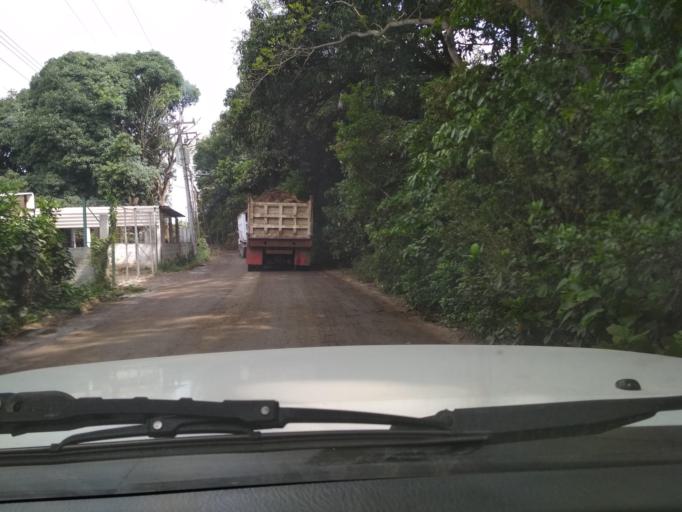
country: MX
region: Veracruz
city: El Tejar
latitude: 19.0836
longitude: -96.1714
